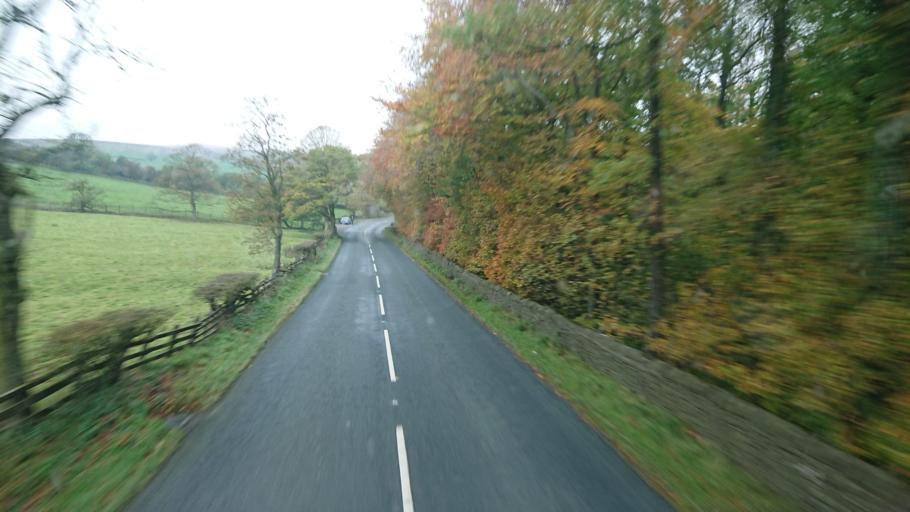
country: GB
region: England
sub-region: North Yorkshire
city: Skipton
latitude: 53.9816
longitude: -2.0325
